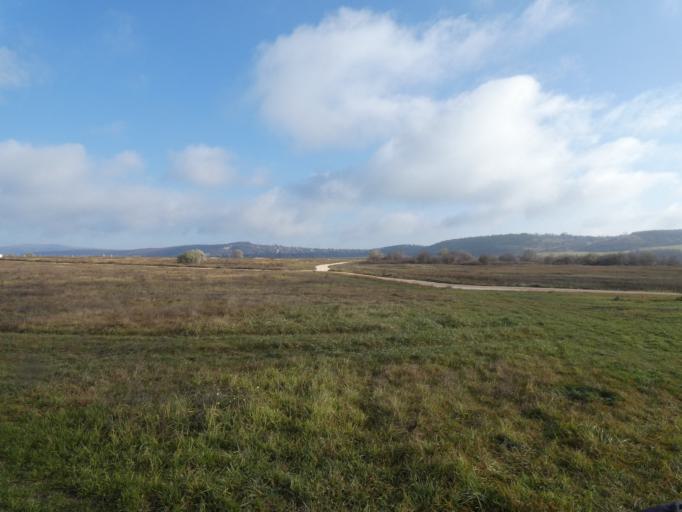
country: HU
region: Pest
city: Paty
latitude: 47.5030
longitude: 18.8313
